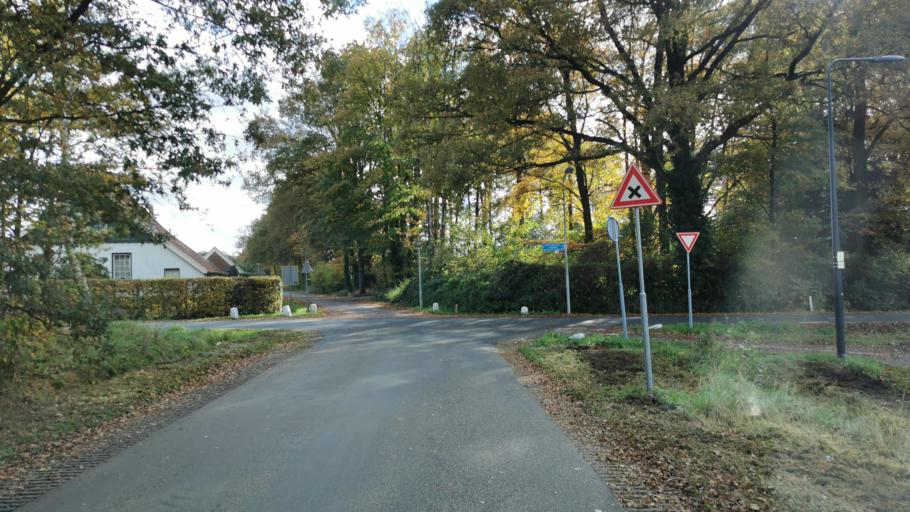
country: NL
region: Overijssel
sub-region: Gemeente Enschede
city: Enschede
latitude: 52.1980
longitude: 6.9189
